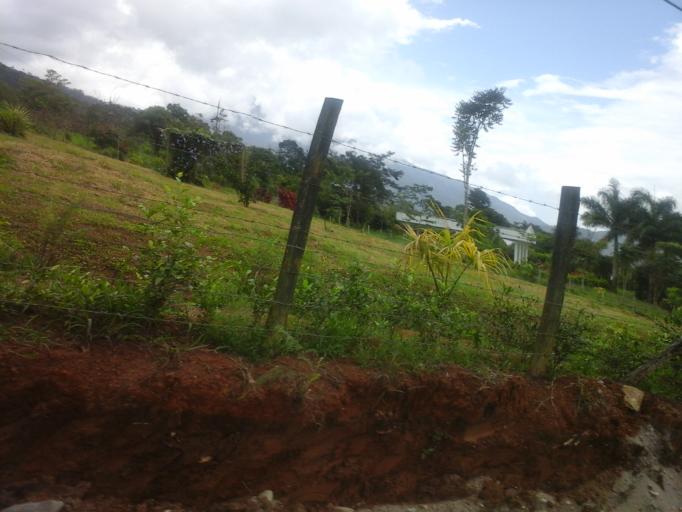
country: CO
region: Putumayo
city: Mocoa
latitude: 1.1759
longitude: -76.6585
